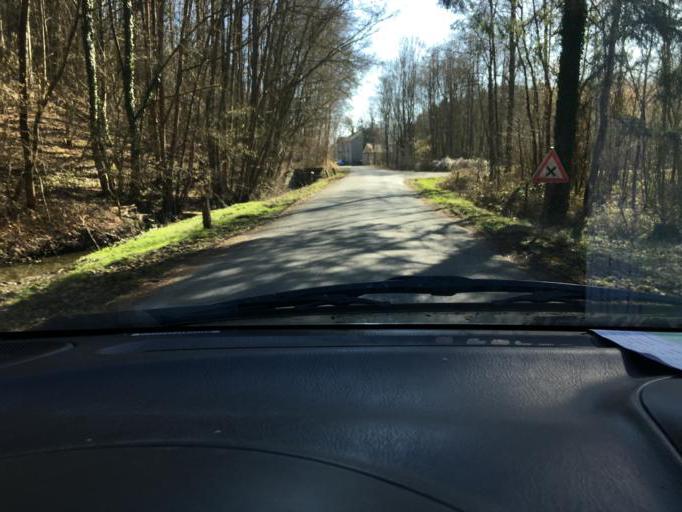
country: BE
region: Wallonia
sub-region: Province de Namur
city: Doische
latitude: 50.1183
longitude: 4.7340
